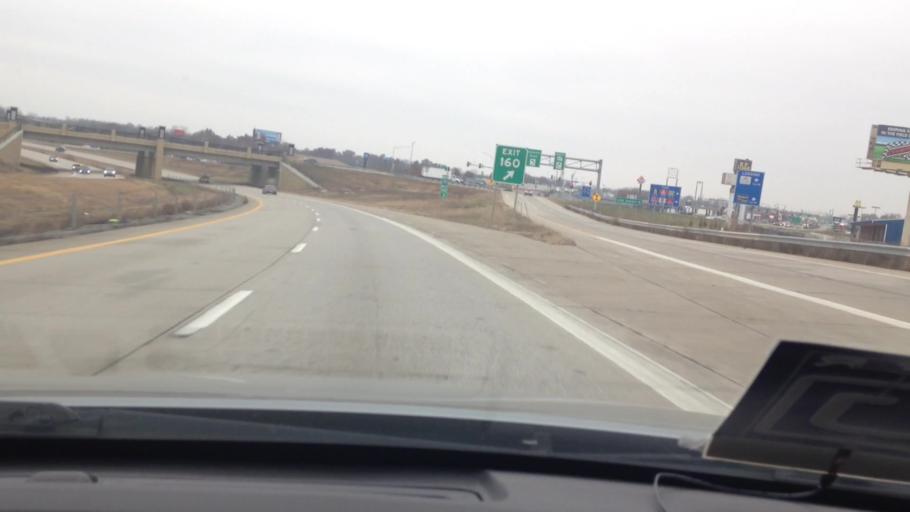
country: US
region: Missouri
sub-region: Cass County
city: Harrisonville
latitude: 38.6590
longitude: -94.3673
